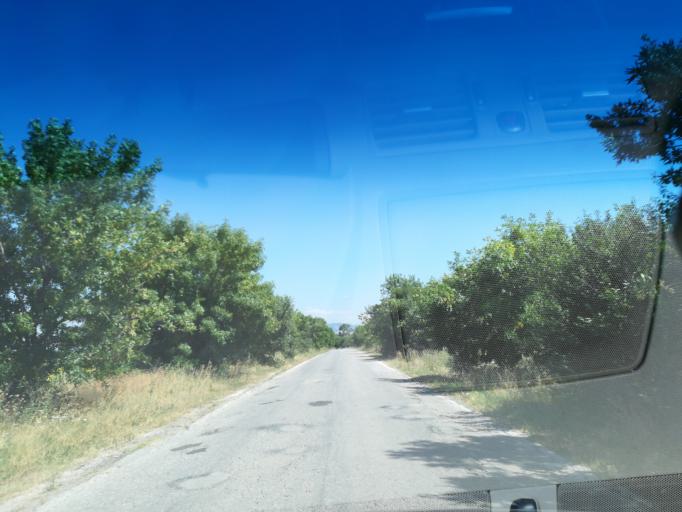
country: BG
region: Plovdiv
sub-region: Obshtina Sadovo
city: Sadovo
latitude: 42.0183
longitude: 25.0289
